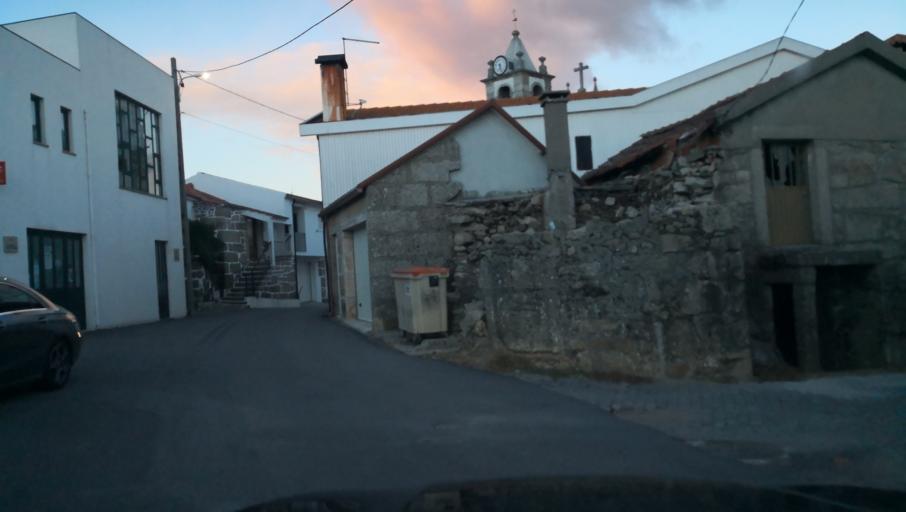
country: PT
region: Vila Real
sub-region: Santa Marta de Penaguiao
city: Santa Marta de Penaguiao
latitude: 41.2736
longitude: -7.8139
